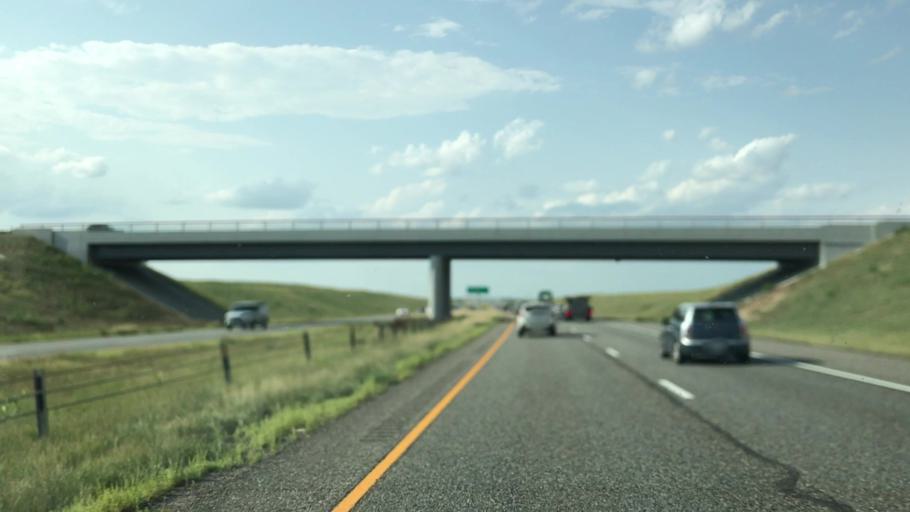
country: US
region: Colorado
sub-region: Arapahoe County
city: Dove Valley
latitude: 39.6521
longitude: -104.7196
